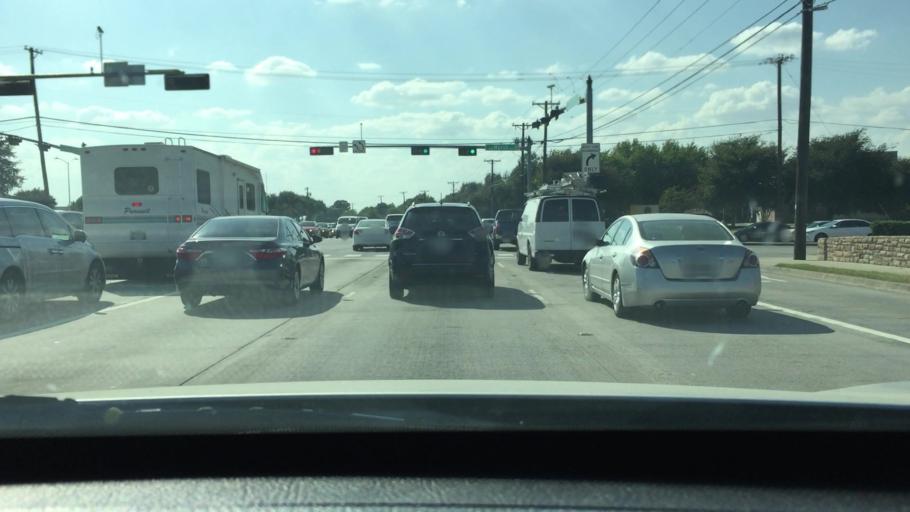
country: US
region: Texas
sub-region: Dallas County
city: Addison
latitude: 32.9871
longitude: -96.8543
